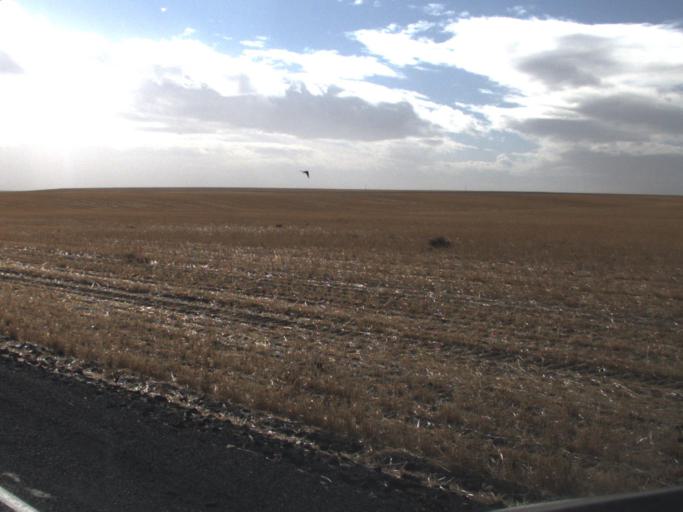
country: US
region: Washington
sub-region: Okanogan County
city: Coulee Dam
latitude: 47.5753
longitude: -118.7859
